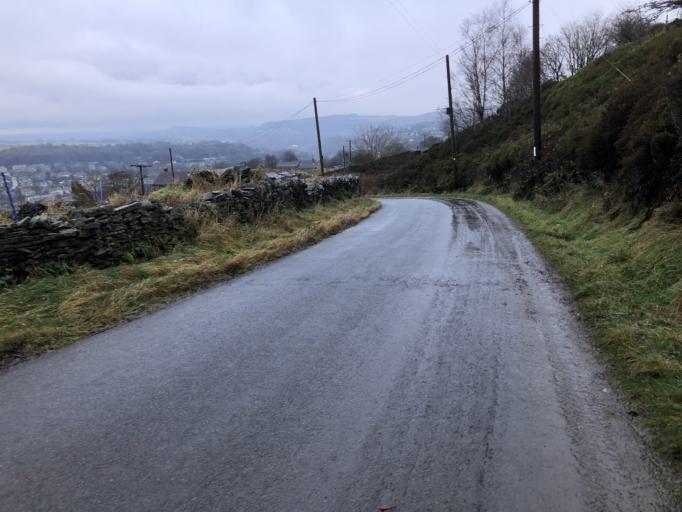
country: GB
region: England
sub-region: Kirklees
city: Holmfirth
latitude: 53.5592
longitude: -1.7985
